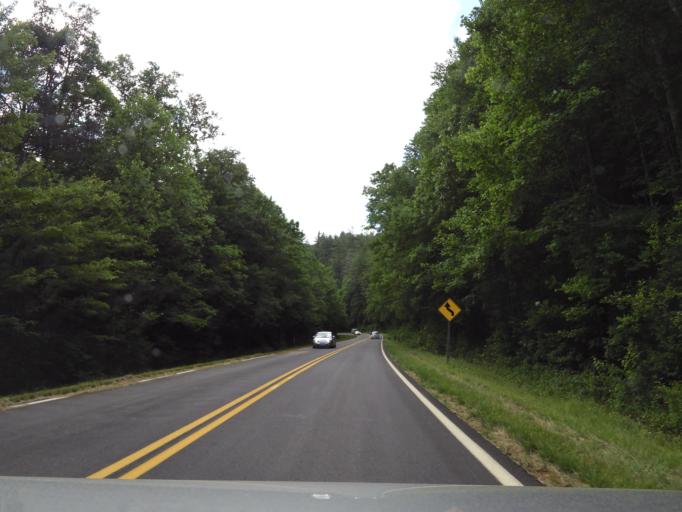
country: US
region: Georgia
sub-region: Towns County
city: Hiawassee
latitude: 34.8358
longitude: -83.7667
